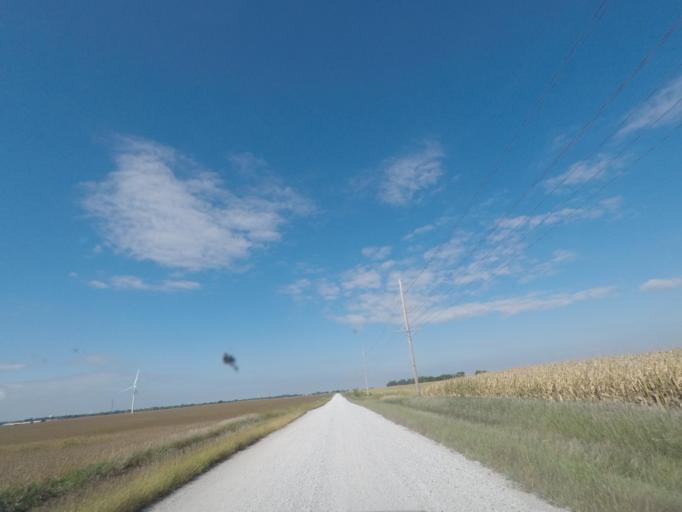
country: US
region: Iowa
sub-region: Story County
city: Nevada
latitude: 42.0344
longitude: -93.4149
